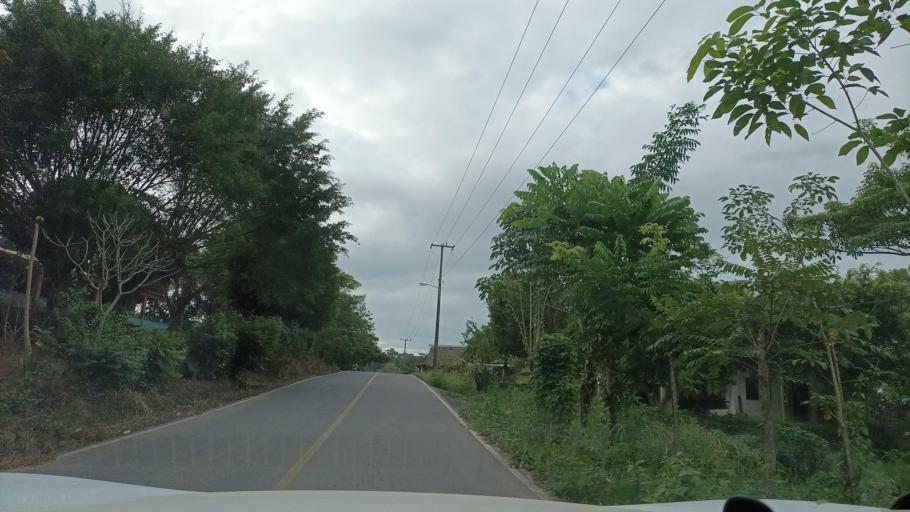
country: MX
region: Veracruz
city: Hidalgotitlan
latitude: 17.7223
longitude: -94.4818
